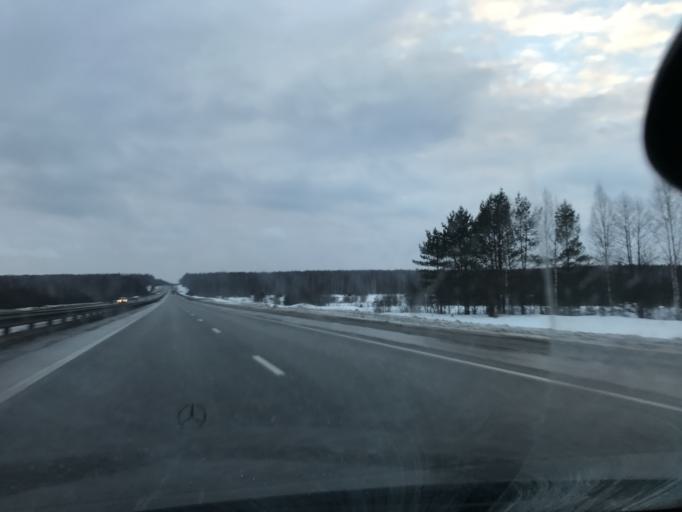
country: RU
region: Vladimir
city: Sudogda
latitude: 56.1278
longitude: 40.8717
